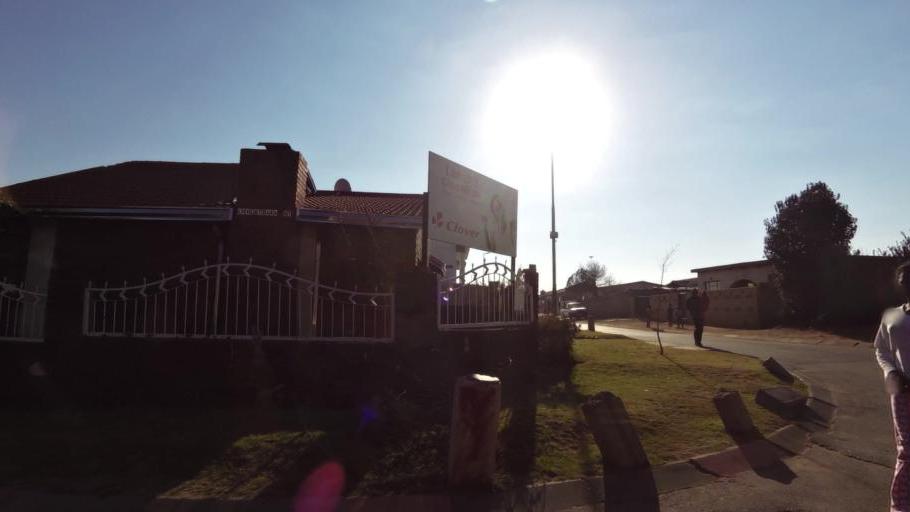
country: ZA
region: Gauteng
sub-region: City of Johannesburg Metropolitan Municipality
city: Soweto
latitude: -26.2315
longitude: 27.9327
